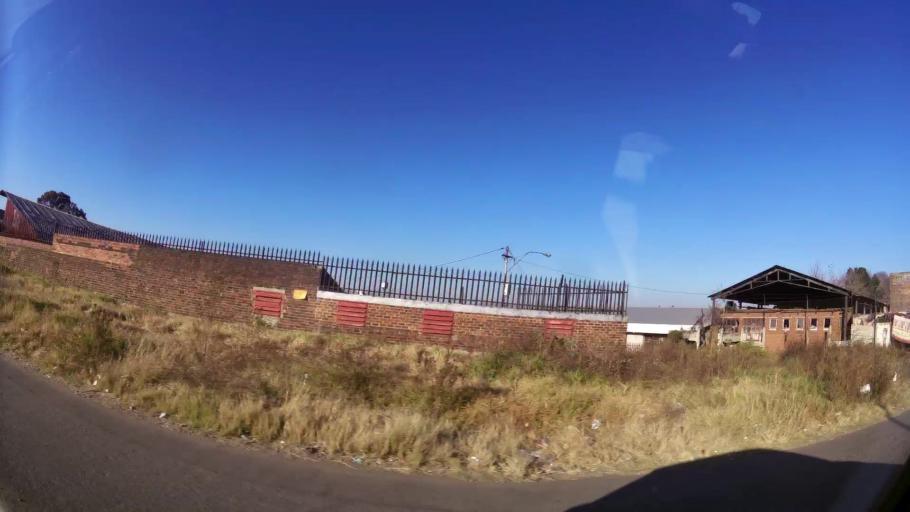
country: ZA
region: Gauteng
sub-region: City of Johannesburg Metropolitan Municipality
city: Johannesburg
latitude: -26.2041
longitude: 28.1083
